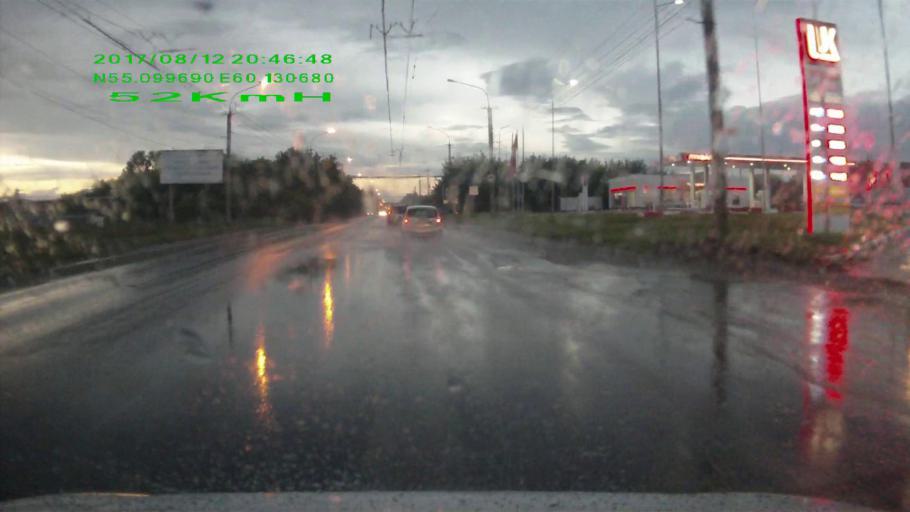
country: RU
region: Chelyabinsk
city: Turgoyak
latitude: 55.0997
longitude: 60.1306
